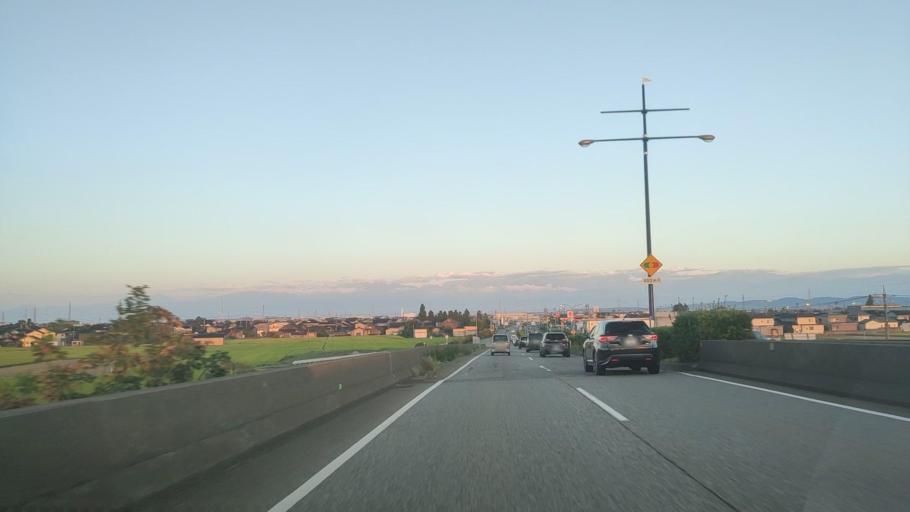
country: JP
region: Toyama
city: Nishishinminato
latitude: 36.7508
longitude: 137.0860
